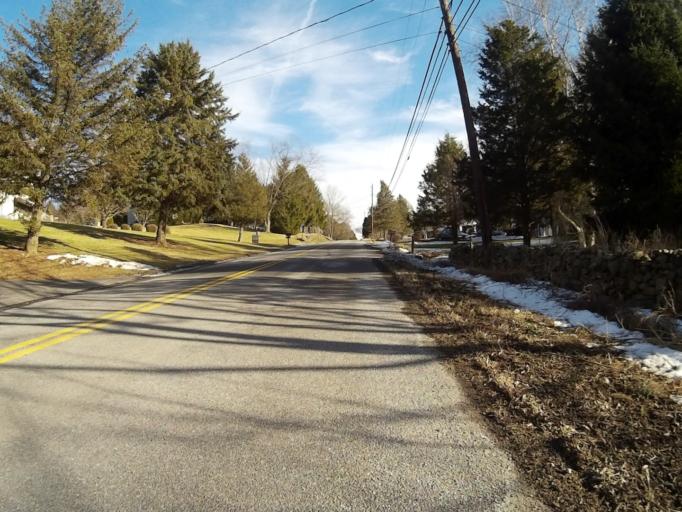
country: US
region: Pennsylvania
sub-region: Centre County
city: Houserville
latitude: 40.8742
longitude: -77.8565
